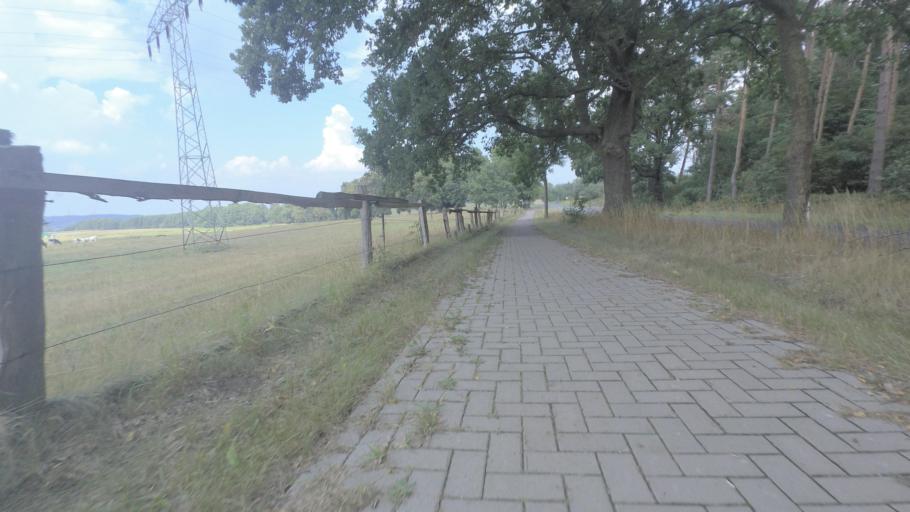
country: DE
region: Mecklenburg-Vorpommern
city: Malchin
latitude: 53.7572
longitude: 12.8368
